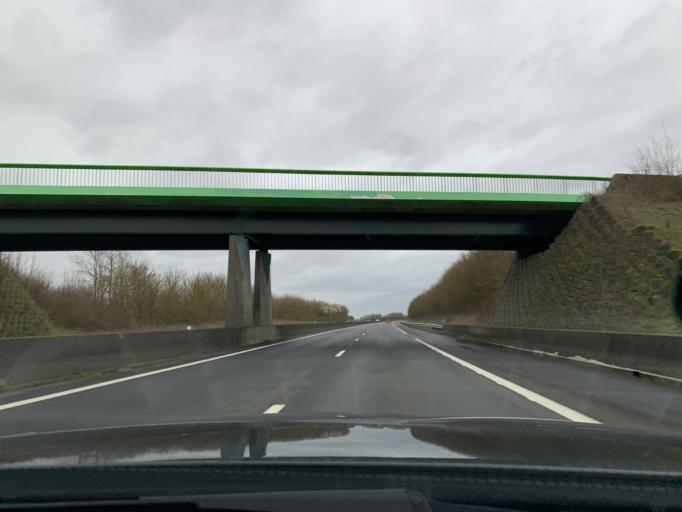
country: FR
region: Picardie
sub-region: Departement de l'Oise
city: Tille
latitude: 49.4930
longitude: 2.1681
